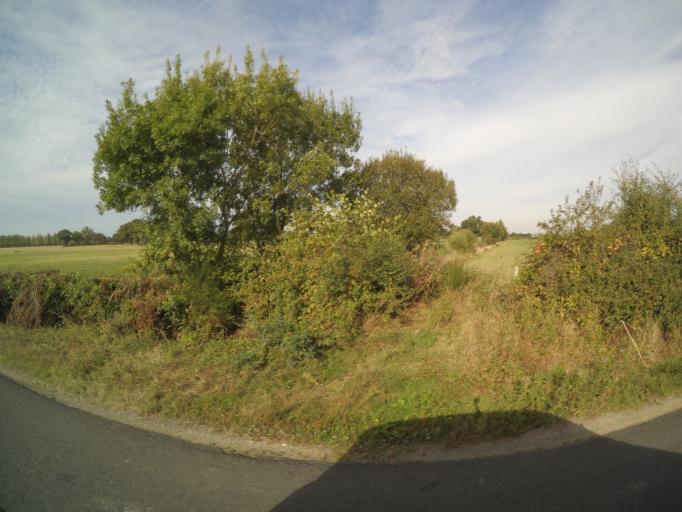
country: FR
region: Pays de la Loire
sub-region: Departement de Maine-et-Loire
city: Tillieres
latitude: 47.1586
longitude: -1.1432
